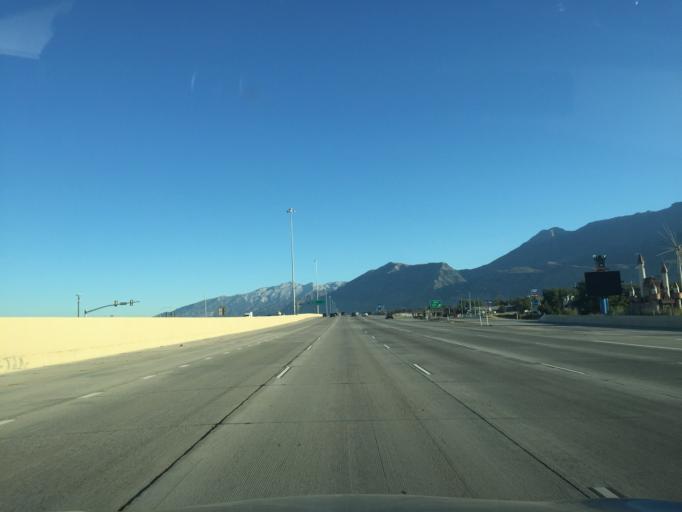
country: US
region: Utah
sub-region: Utah County
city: Orem
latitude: 40.2938
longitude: -111.7255
